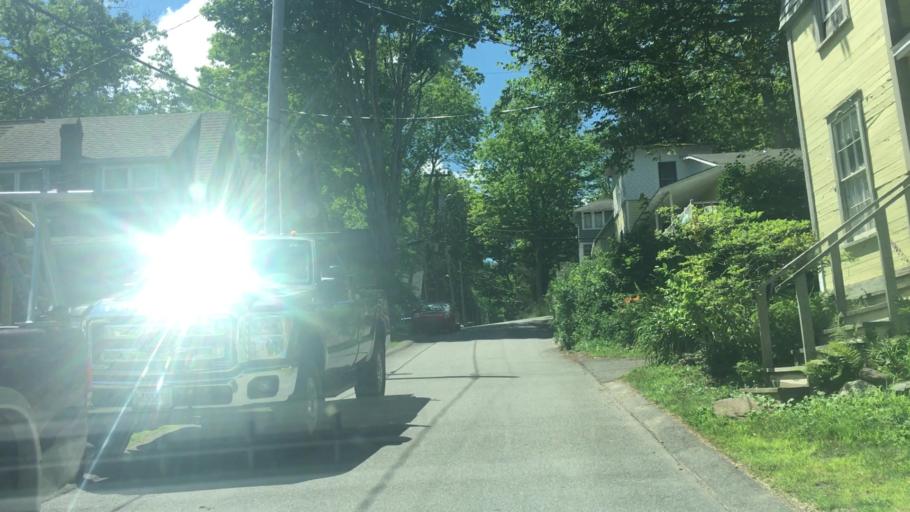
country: US
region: Maine
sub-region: Waldo County
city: Northport
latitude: 44.3796
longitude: -68.9689
